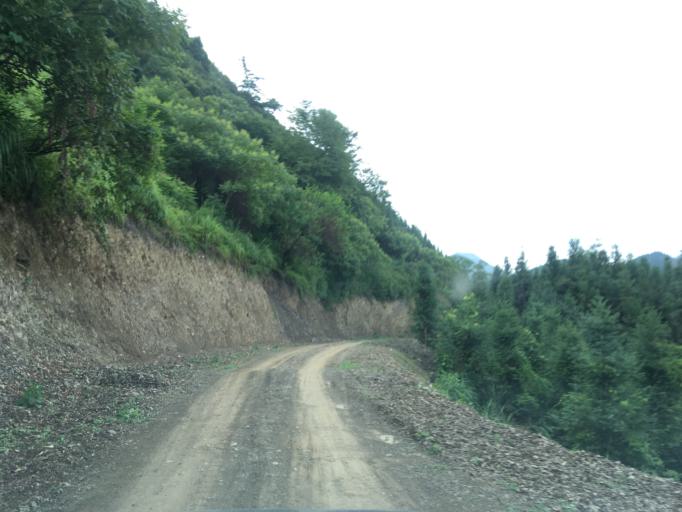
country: CN
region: Guangxi Zhuangzu Zizhiqu
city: Xinzhou
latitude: 24.8731
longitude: 105.8457
